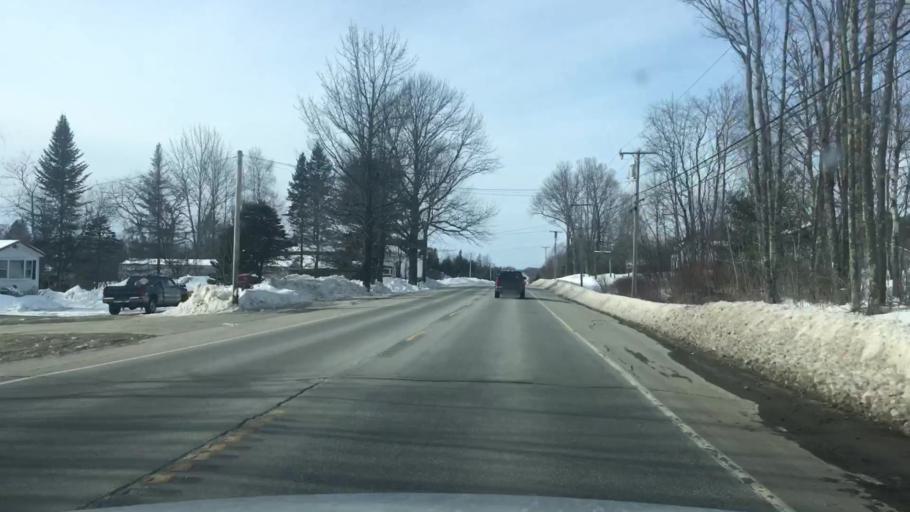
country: US
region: Maine
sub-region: Penobscot County
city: Kenduskeag
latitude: 44.9738
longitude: -68.9828
